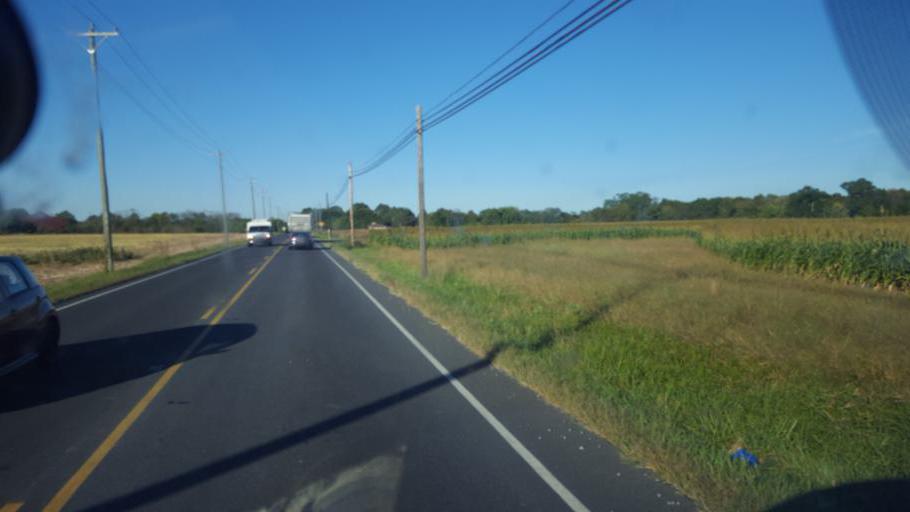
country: US
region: Virginia
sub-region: Prince William County
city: Nokesville
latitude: 38.6379
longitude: -77.6679
